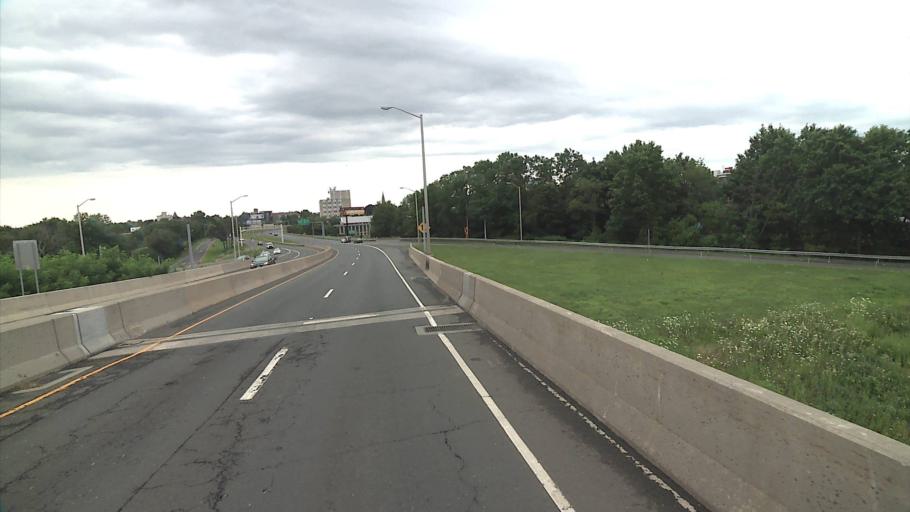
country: US
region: Connecticut
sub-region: Fairfield County
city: Bridgeport
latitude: 41.1718
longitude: -73.1927
